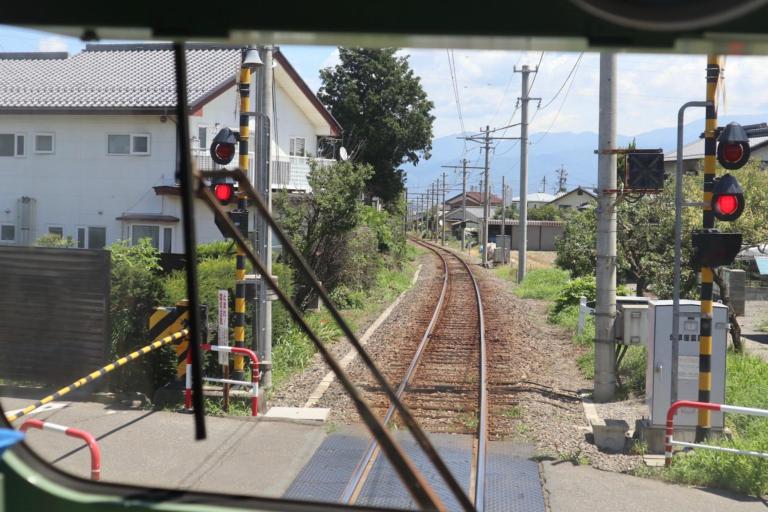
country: JP
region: Nagano
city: Matsumoto
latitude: 36.2085
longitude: 137.8825
